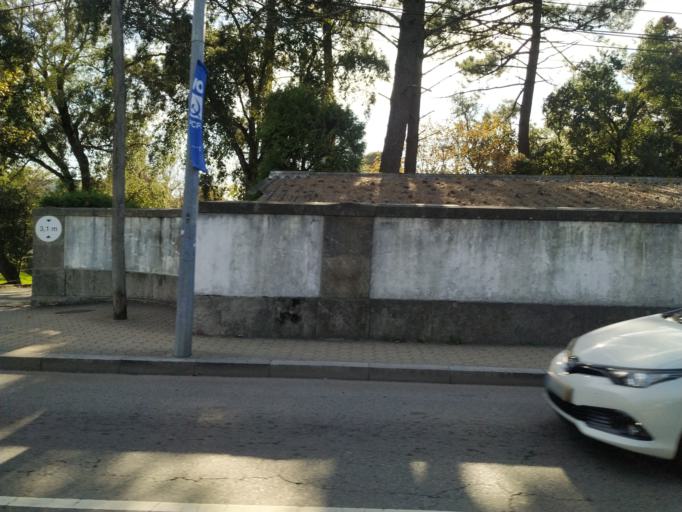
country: PT
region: Porto
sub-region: Vila Nova de Gaia
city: Vilar de Andorinho
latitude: 41.1062
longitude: -8.5918
